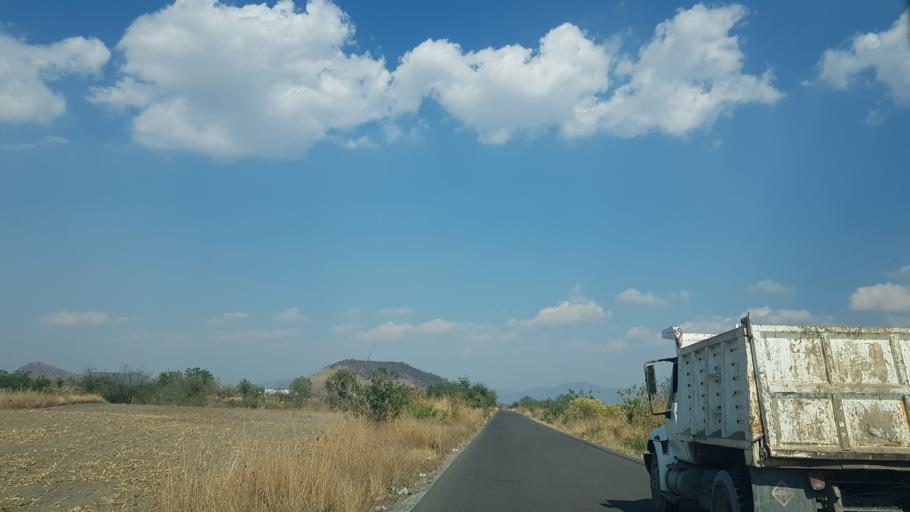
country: MX
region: Puebla
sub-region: Atlixco
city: Colonia Agricola de Ocotepec (Colonia San Jose)
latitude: 18.9236
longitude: -98.4966
